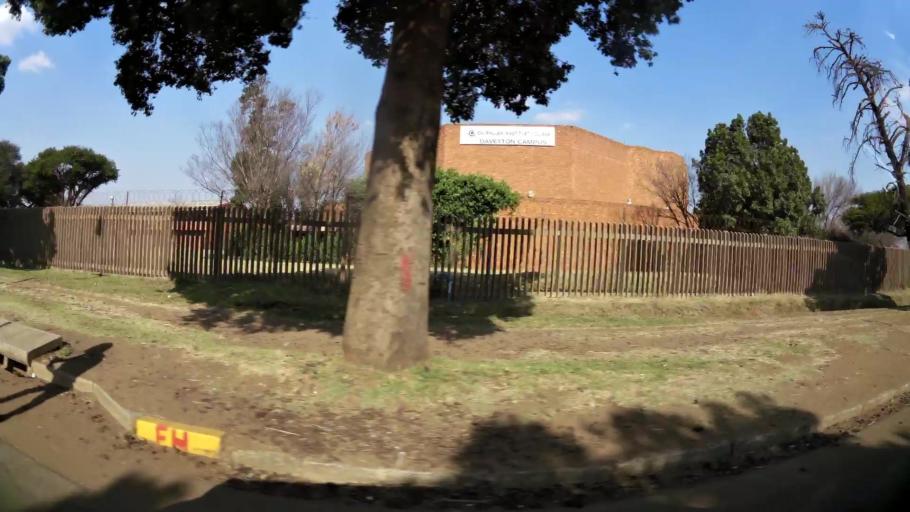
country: ZA
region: Gauteng
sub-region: Ekurhuleni Metropolitan Municipality
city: Brakpan
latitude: -26.1573
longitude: 28.4155
